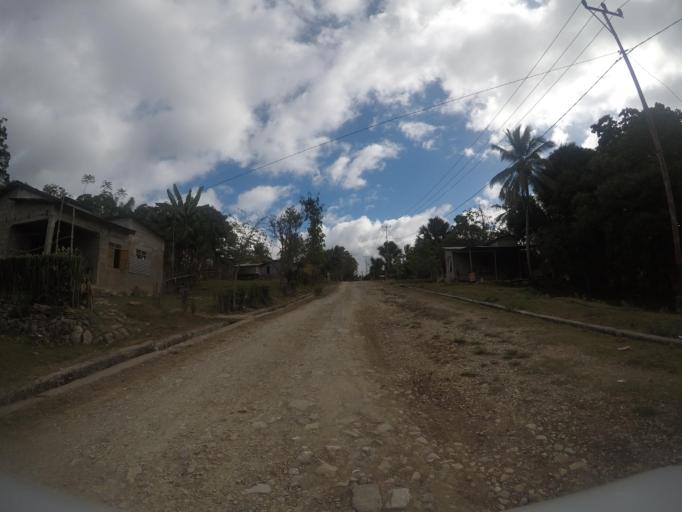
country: TL
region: Lautem
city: Lospalos
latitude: -8.5664
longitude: 126.8862
